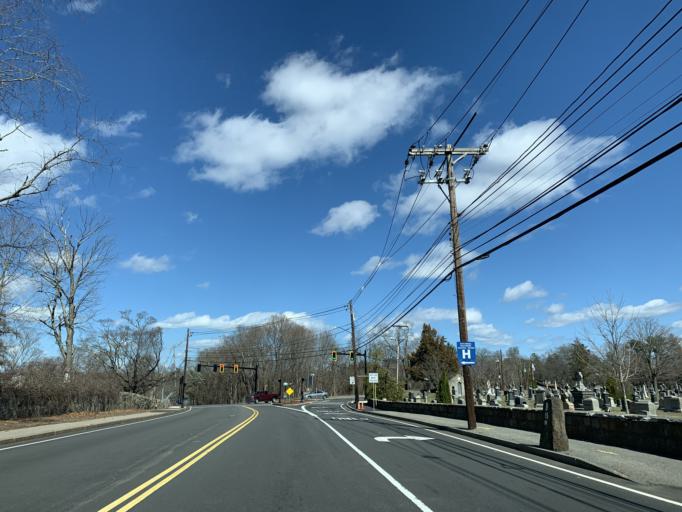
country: US
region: Massachusetts
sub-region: Norfolk County
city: Canton
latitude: 42.1759
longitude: -71.1322
